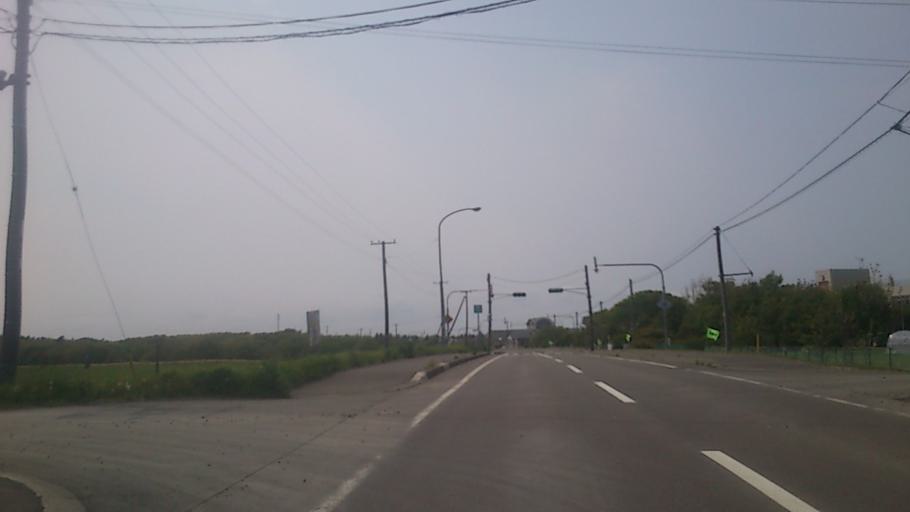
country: JP
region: Hokkaido
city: Nemuro
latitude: 43.2782
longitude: 145.5203
